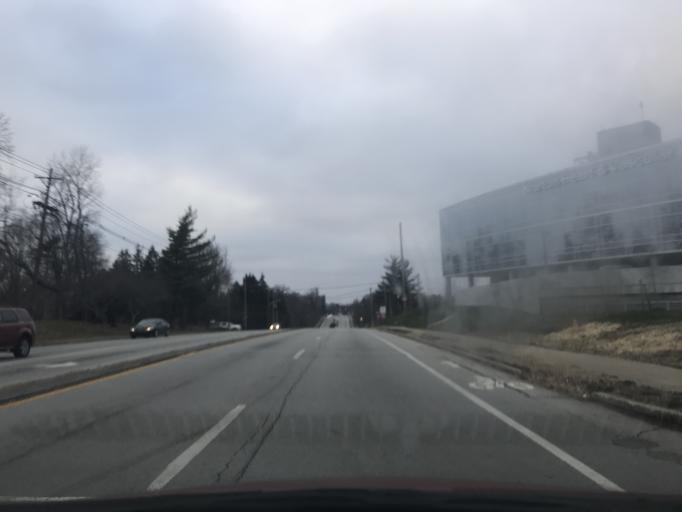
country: US
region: Kentucky
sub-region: Jefferson County
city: Audubon Park
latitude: 38.2141
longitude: -85.7230
